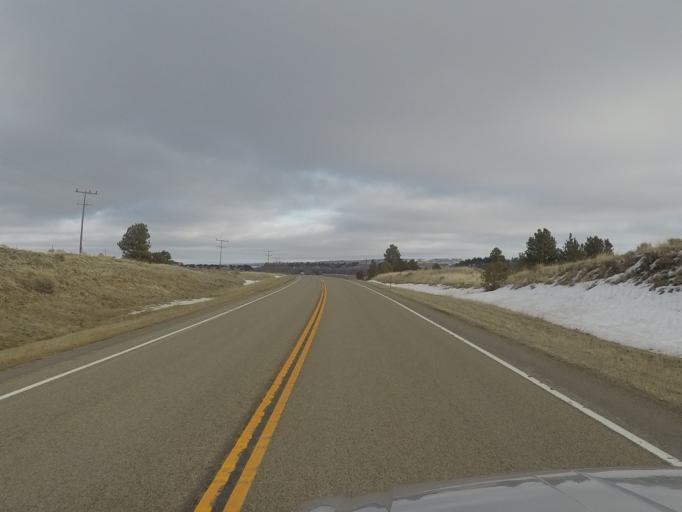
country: US
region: Montana
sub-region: Golden Valley County
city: Ryegate
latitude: 46.3005
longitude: -109.3280
